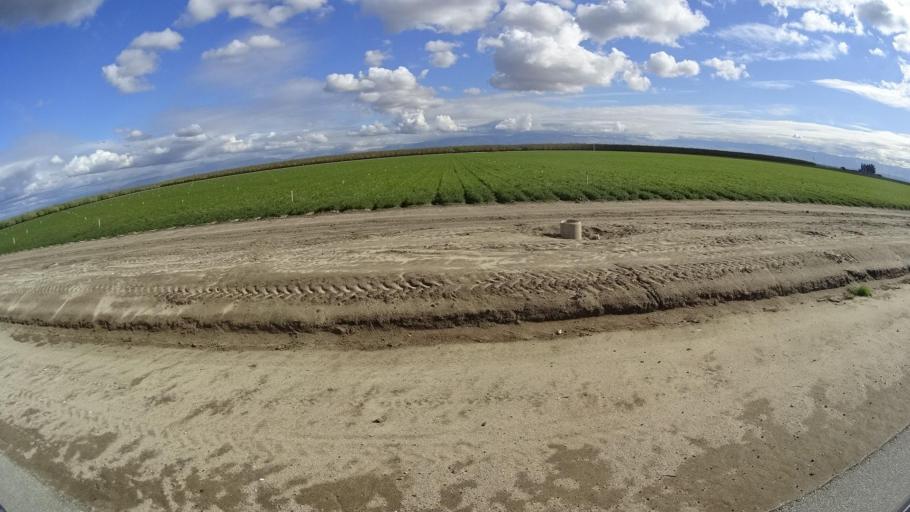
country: US
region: California
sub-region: Kern County
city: Greenfield
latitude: 35.2203
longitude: -119.0746
